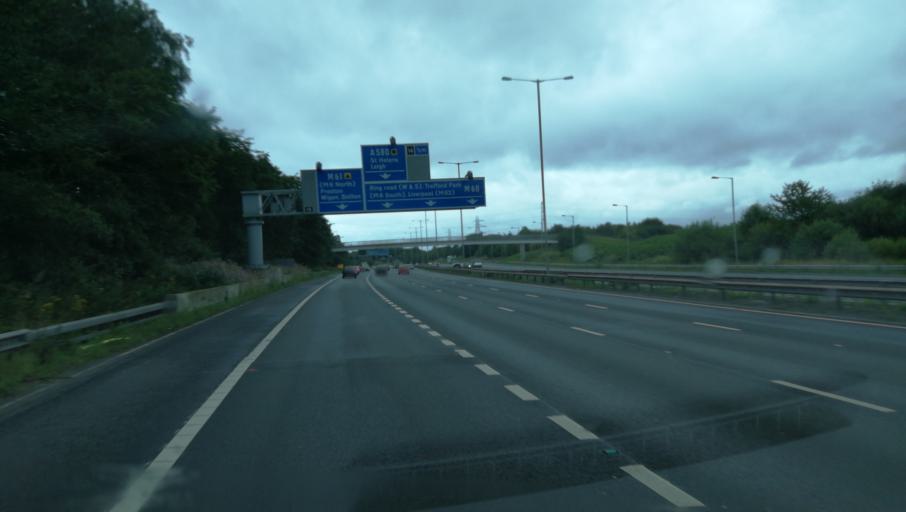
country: GB
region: England
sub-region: Manchester
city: Swinton
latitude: 53.5247
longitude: -2.3470
